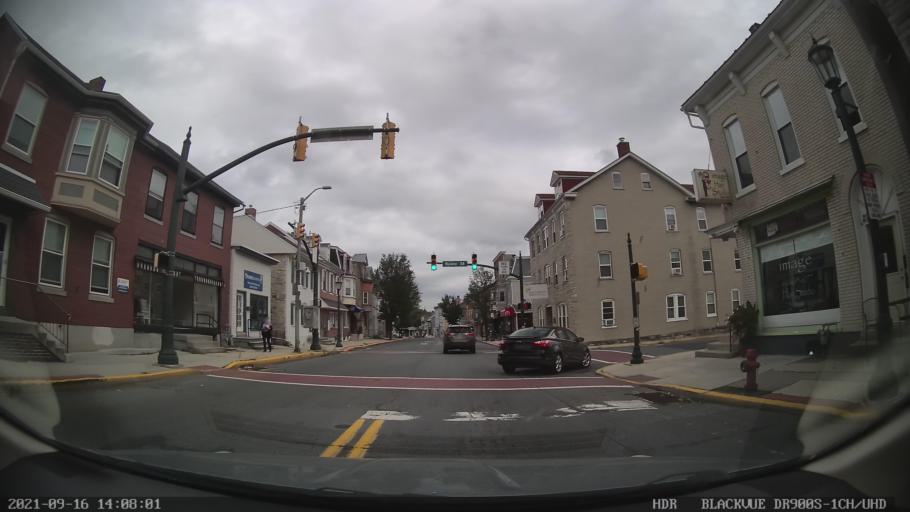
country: US
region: Pennsylvania
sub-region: Berks County
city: Kutztown
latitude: 40.5174
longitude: -75.7773
